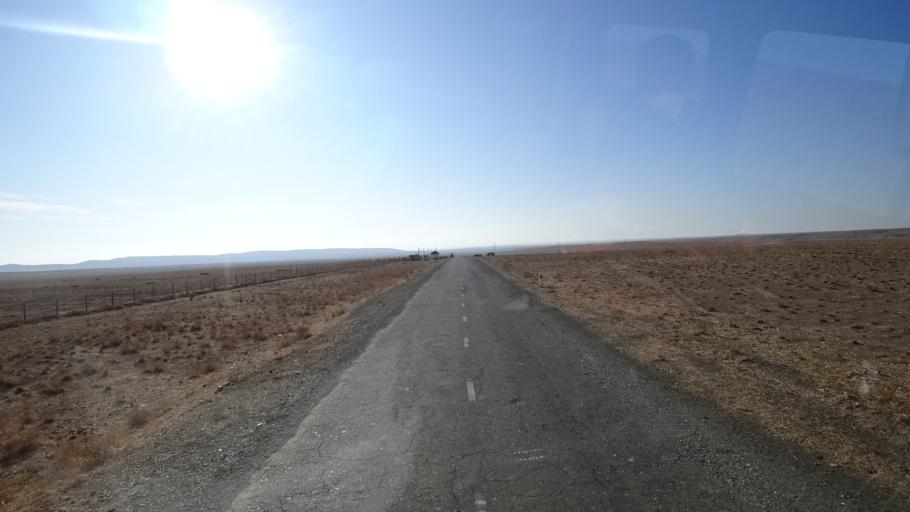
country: UZ
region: Navoiy
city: Karmana Shahri
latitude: 40.2745
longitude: 65.5419
